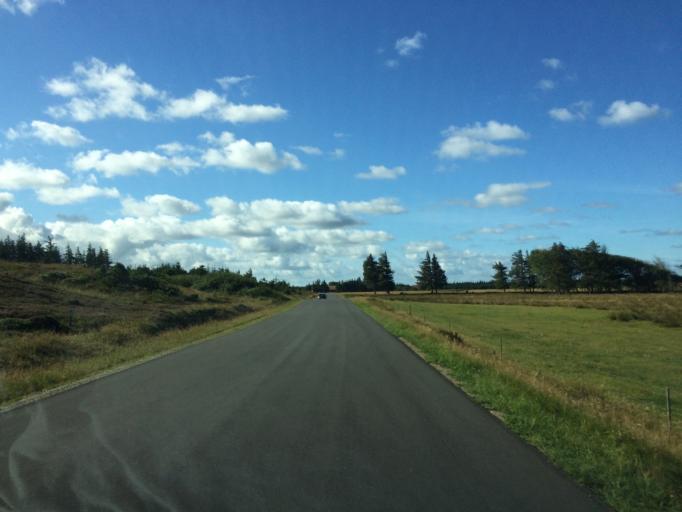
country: DK
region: South Denmark
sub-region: Varde Kommune
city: Oksbol
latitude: 55.6475
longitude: 8.1785
